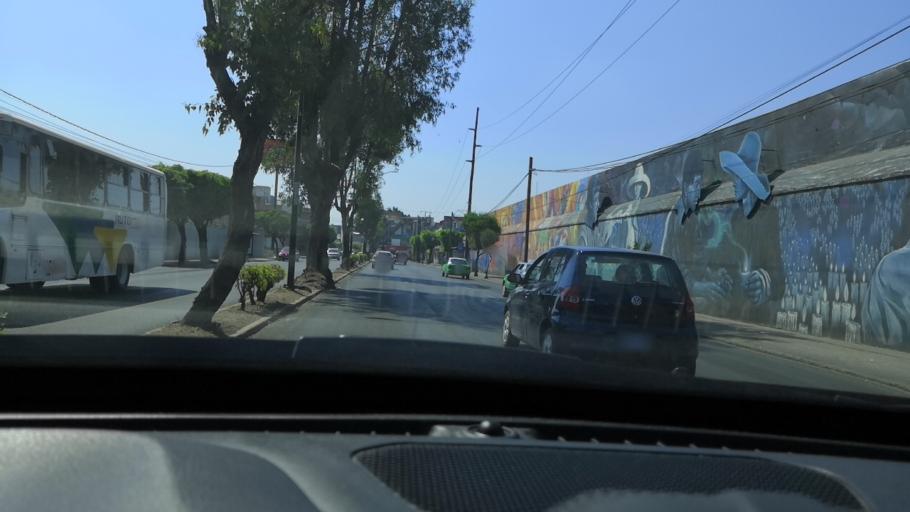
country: MX
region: Guanajuato
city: Leon
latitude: 21.1131
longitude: -101.6777
